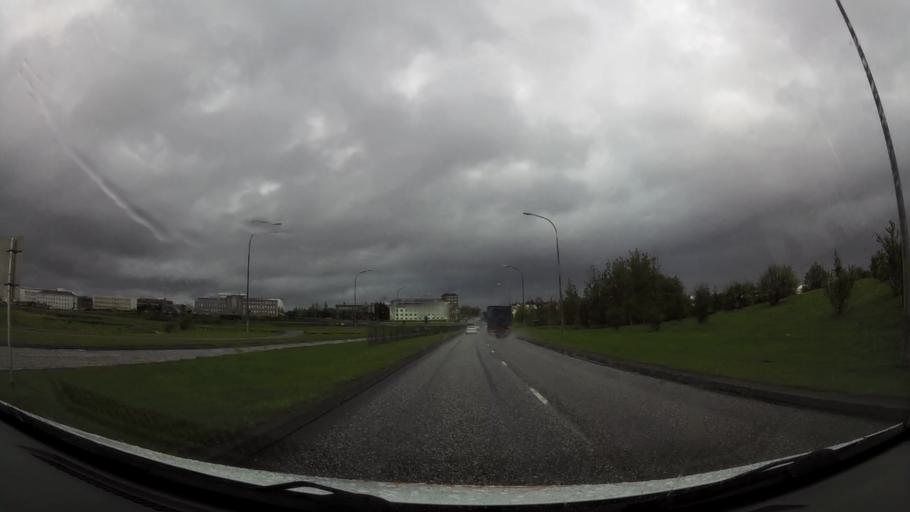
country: IS
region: Capital Region
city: Kopavogur
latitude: 64.1394
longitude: -21.9417
